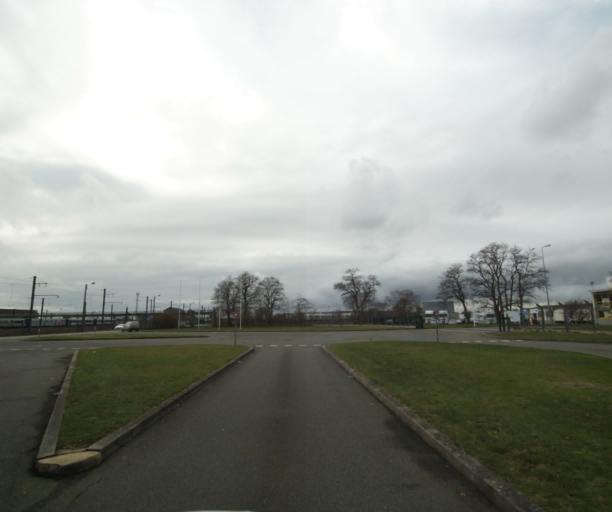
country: FR
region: Pays de la Loire
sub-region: Departement de la Sarthe
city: Le Mans
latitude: 47.9753
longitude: 0.1940
